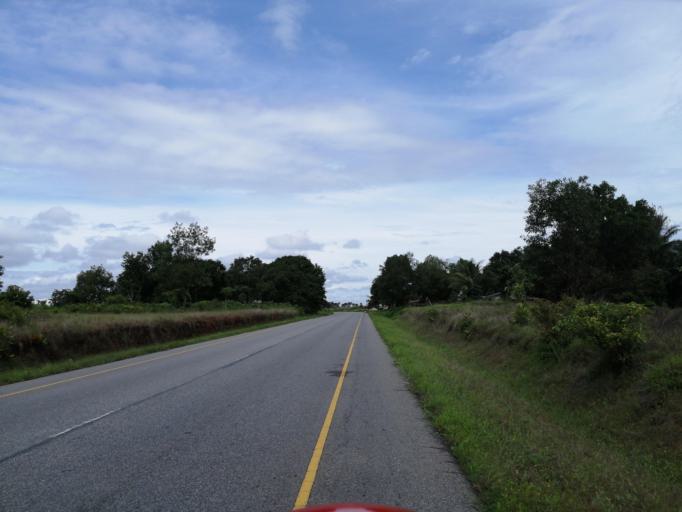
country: SL
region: Northern Province
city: Port Loko
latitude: 8.7371
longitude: -12.9461
